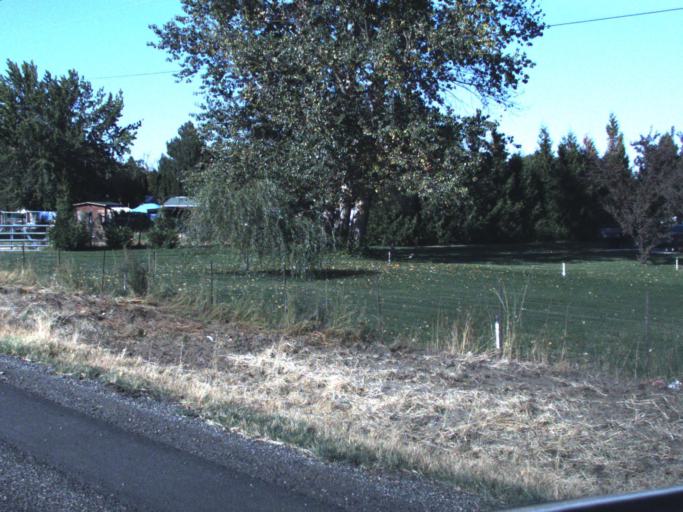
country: US
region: Washington
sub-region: Benton County
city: Finley
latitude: 46.1508
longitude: -119.0254
